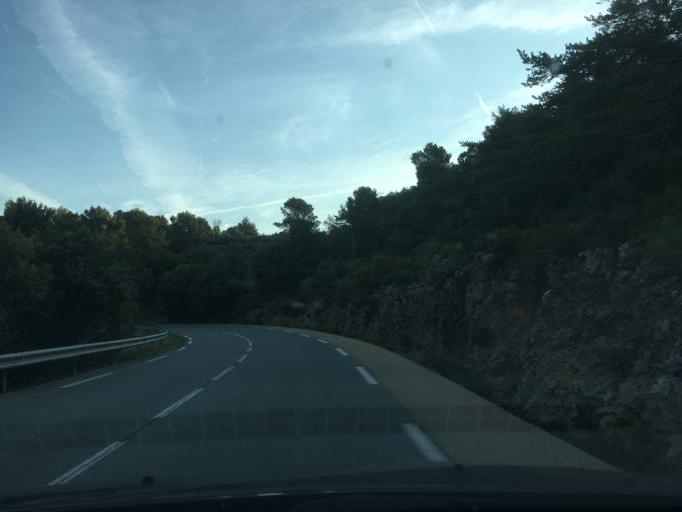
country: FR
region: Provence-Alpes-Cote d'Azur
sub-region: Departement du Var
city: Aups
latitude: 43.6558
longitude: 6.2234
